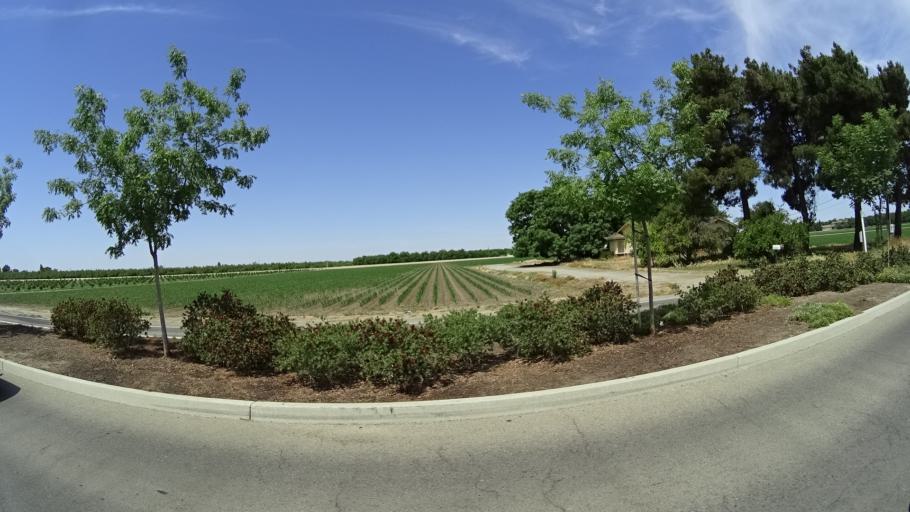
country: US
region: California
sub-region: Kings County
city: Armona
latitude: 36.3321
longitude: -119.6909
